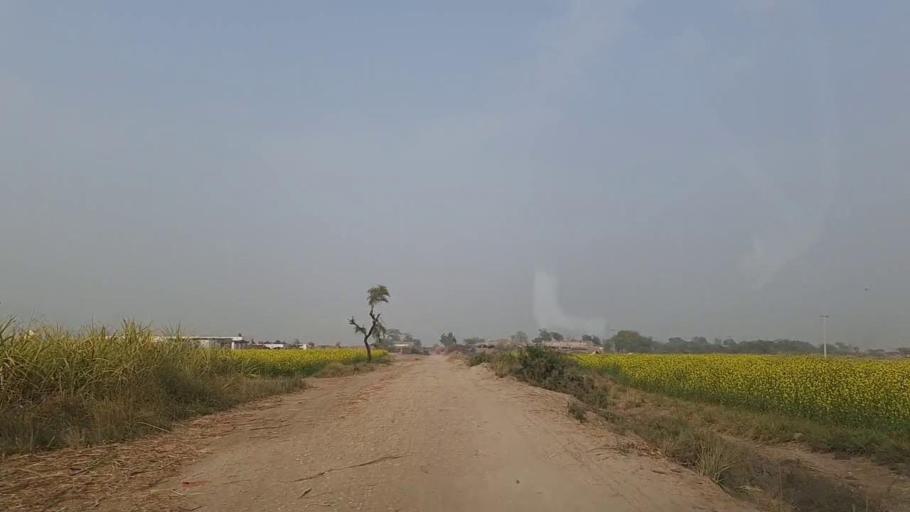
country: PK
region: Sindh
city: Sanghar
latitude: 26.1164
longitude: 68.8963
